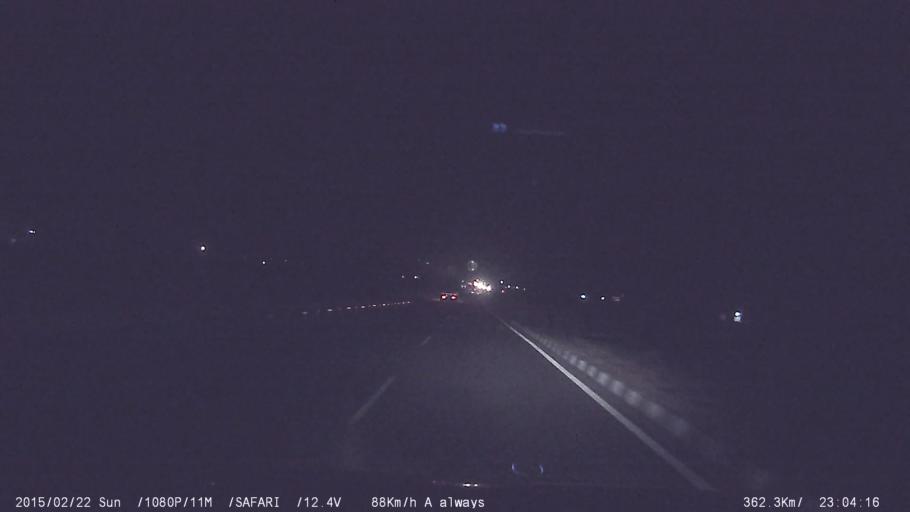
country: IN
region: Tamil Nadu
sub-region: Namakkal
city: Rasipuram
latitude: 11.4001
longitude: 78.1599
